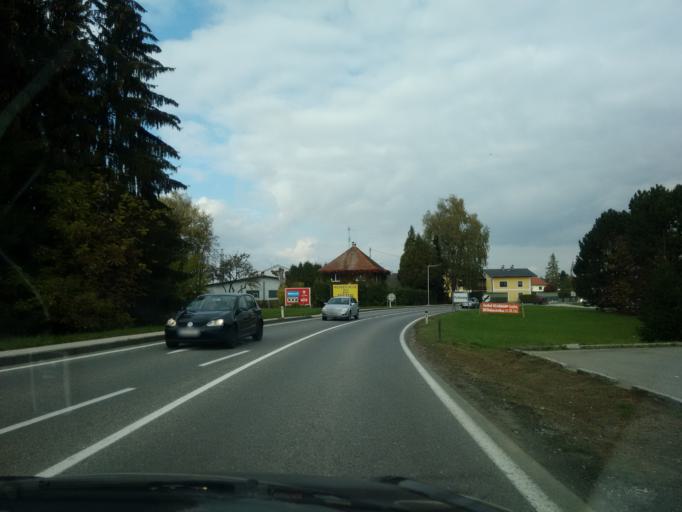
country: AT
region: Upper Austria
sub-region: Politischer Bezirk Vocklabruck
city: Lenzing
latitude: 47.9840
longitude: 13.6138
